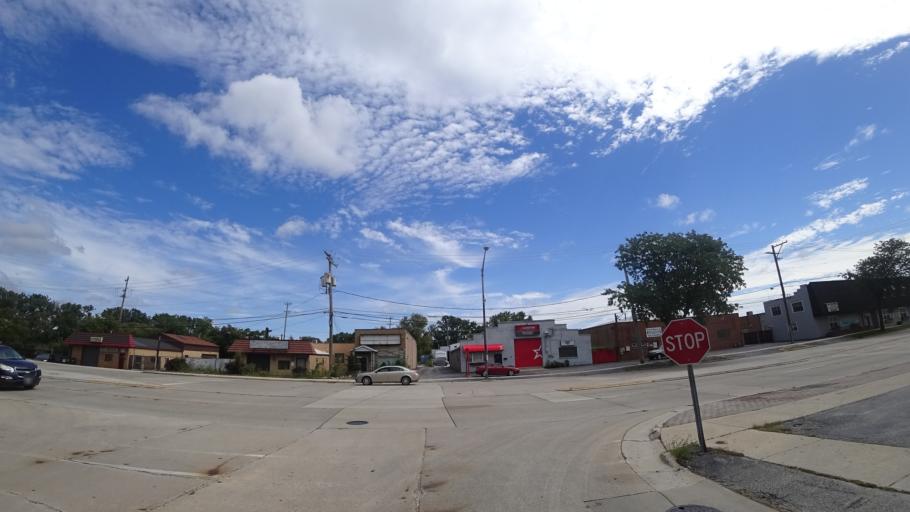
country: US
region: Illinois
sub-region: Cook County
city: Chicago Ridge
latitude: 41.7059
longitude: -87.7797
